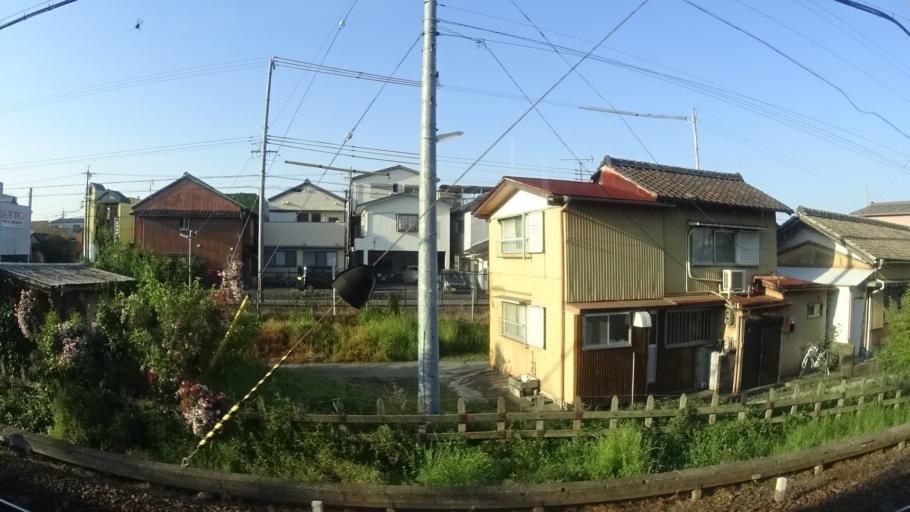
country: JP
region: Mie
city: Ise
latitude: 34.4971
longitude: 136.7000
